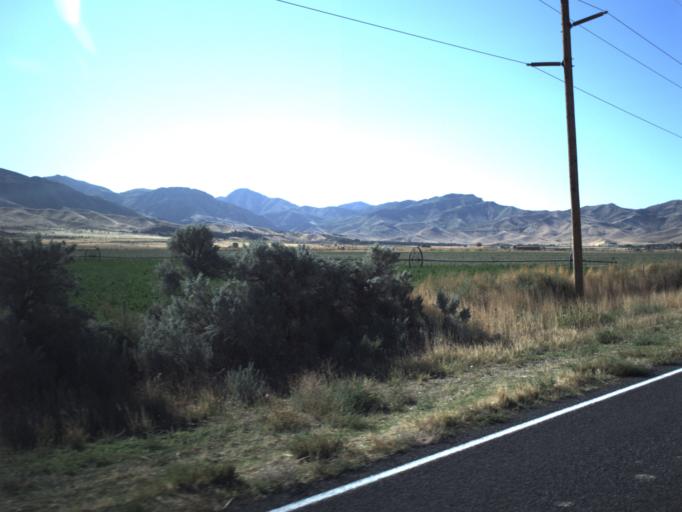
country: US
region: Utah
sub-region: Millard County
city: Delta
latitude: 39.4124
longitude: -112.3310
